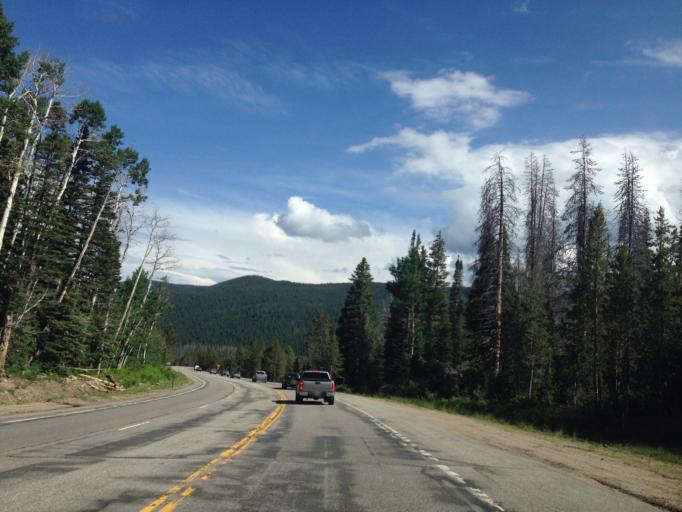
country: US
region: Colorado
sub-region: Routt County
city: Steamboat Springs
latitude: 40.3553
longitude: -106.7497
